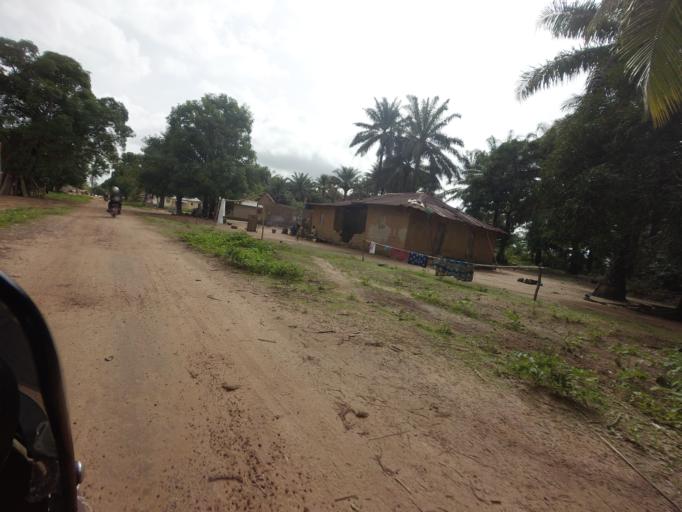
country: SL
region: Northern Province
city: Kambia
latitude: 9.0750
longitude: -13.0369
